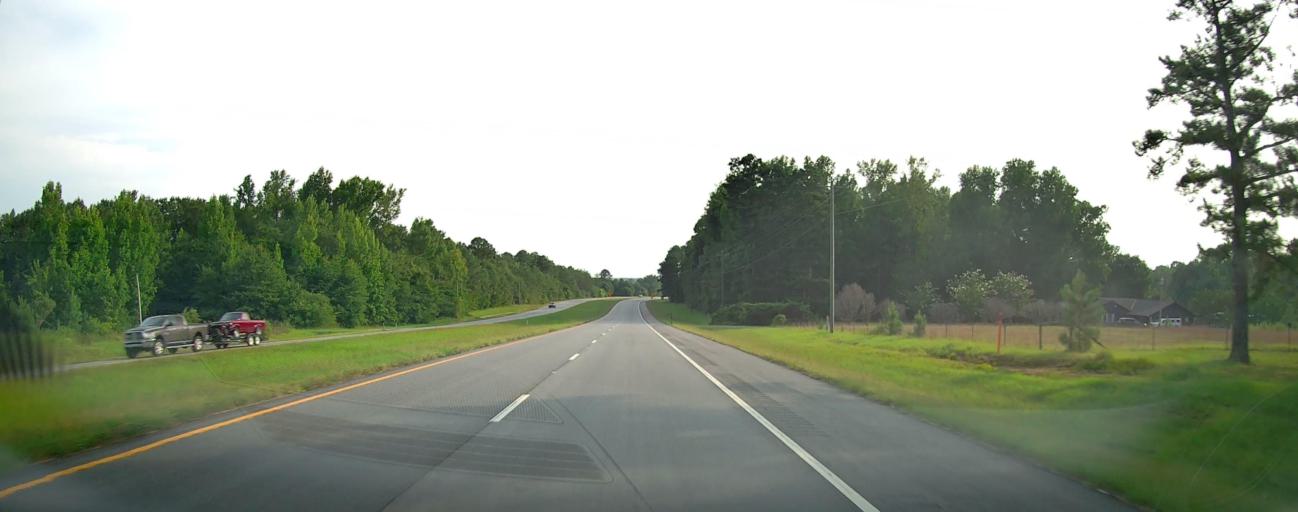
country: US
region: Georgia
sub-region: Talbot County
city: Talbotton
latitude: 32.5677
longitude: -84.6023
